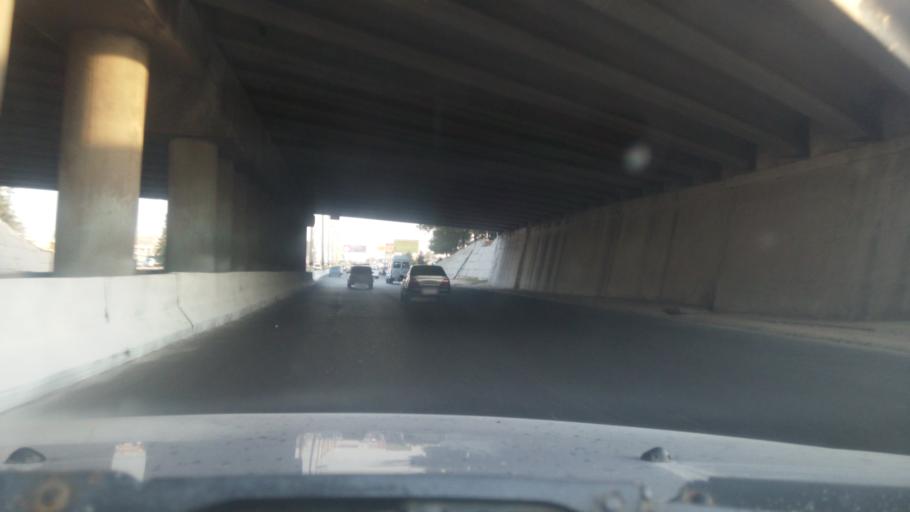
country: UZ
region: Toshkent Shahri
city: Tashkent
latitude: 41.2383
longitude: 69.1679
